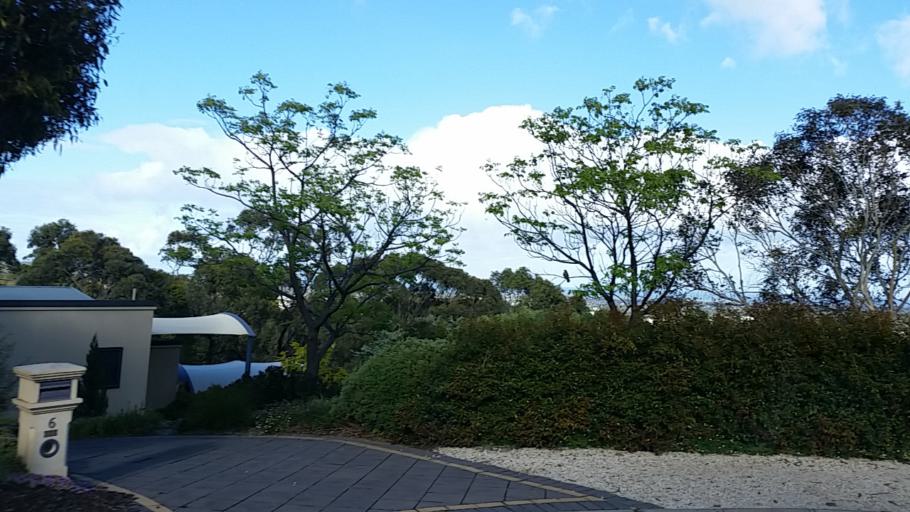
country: AU
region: South Australia
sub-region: Mitcham
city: Clapham
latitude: -35.0115
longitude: 138.5917
